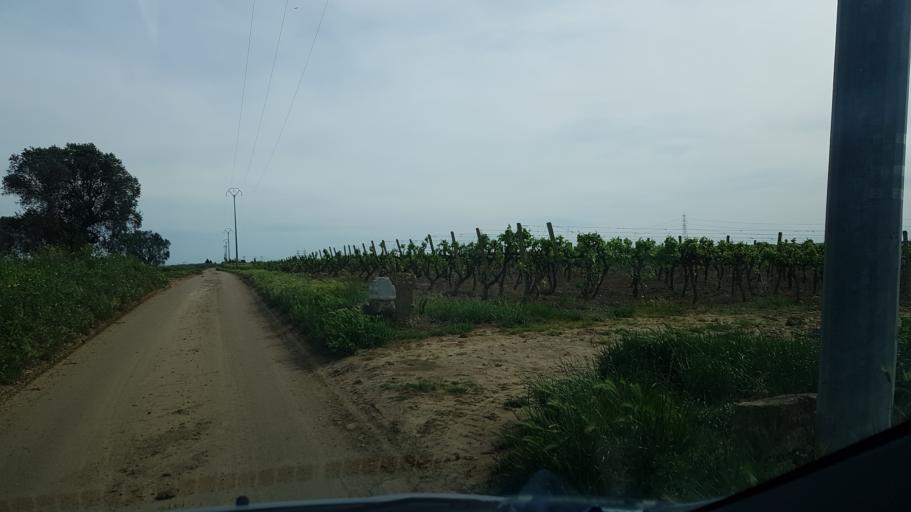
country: IT
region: Apulia
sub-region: Provincia di Brindisi
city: Tuturano
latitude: 40.5741
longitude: 17.9206
